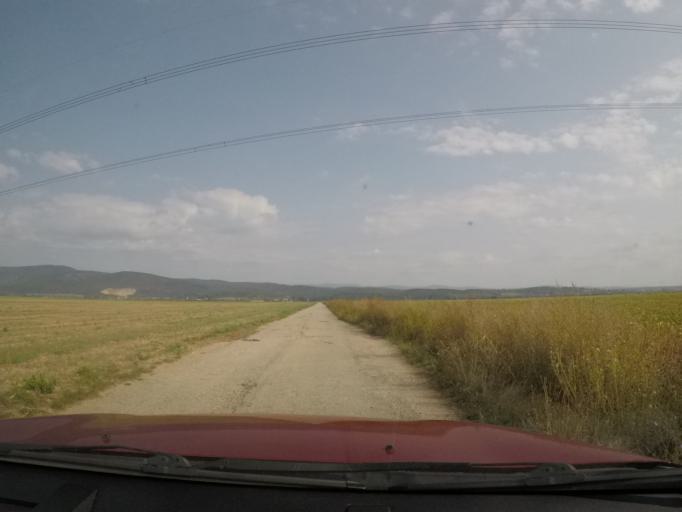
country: SK
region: Kosicky
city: Moldava nad Bodvou
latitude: 48.5870
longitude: 20.9568
